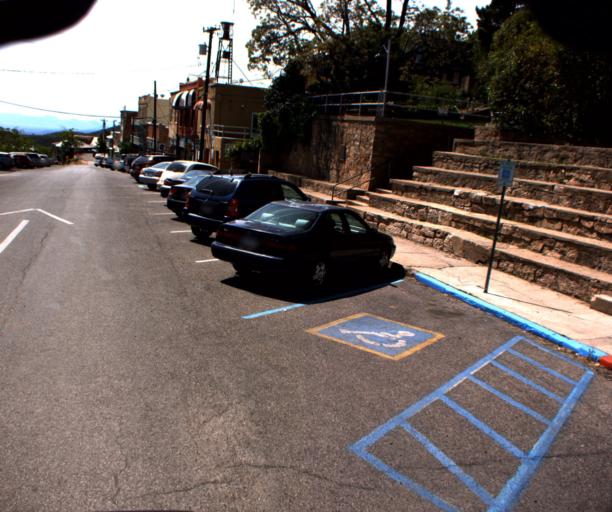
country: US
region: Arizona
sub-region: Yavapai County
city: Clarkdale
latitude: 34.7510
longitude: -112.1162
